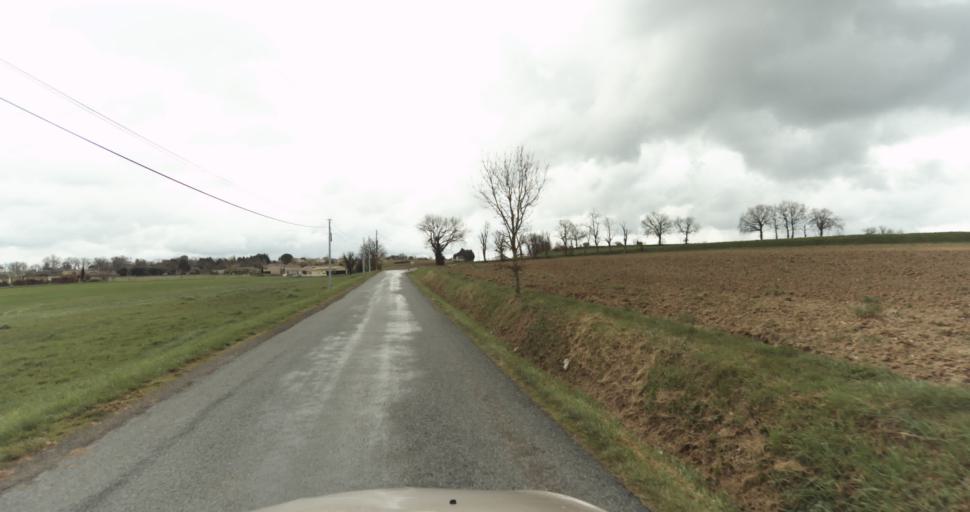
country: FR
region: Midi-Pyrenees
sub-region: Departement du Tarn
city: Frejairolles
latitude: 43.8527
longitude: 2.1972
